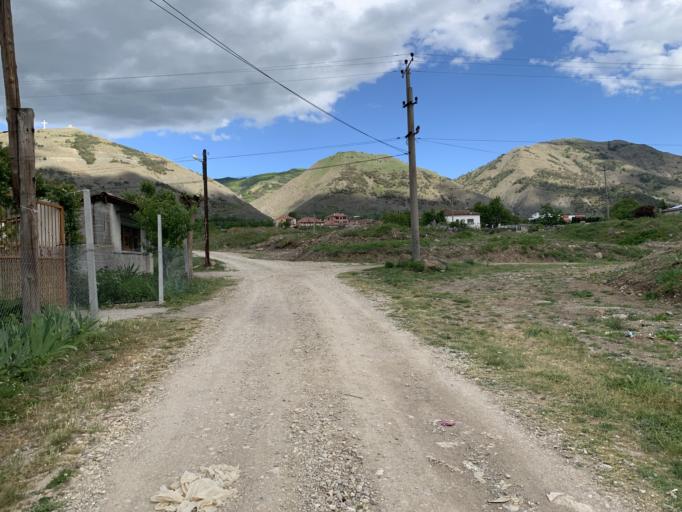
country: AL
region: Korce
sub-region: Rrethi i Korces
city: Korce
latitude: 40.6117
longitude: 20.7925
